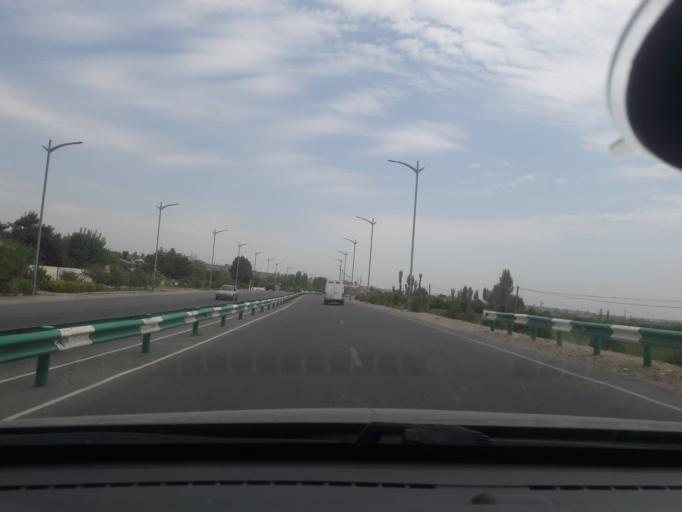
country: TJ
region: Republican Subordination
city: Hisor
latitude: 38.5532
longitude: 68.5785
